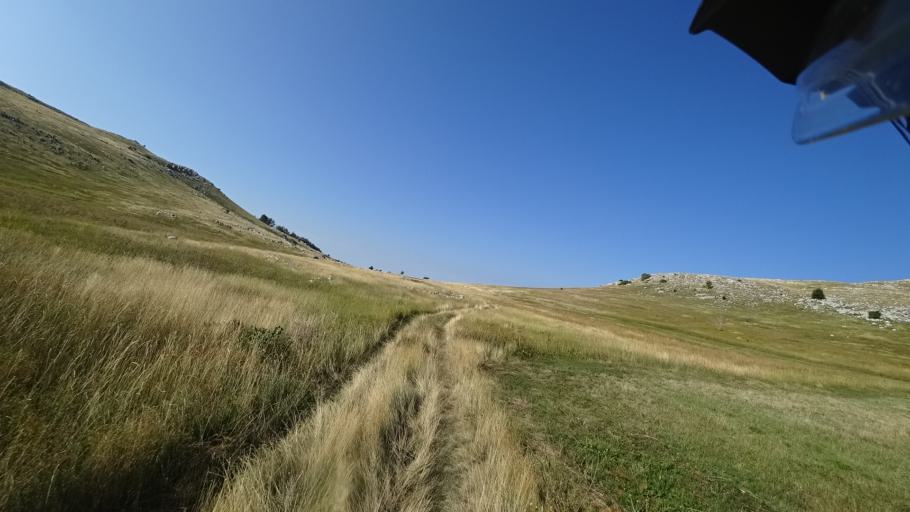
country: HR
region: Sibensko-Kniniska
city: Knin
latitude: 44.2022
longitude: 16.1359
